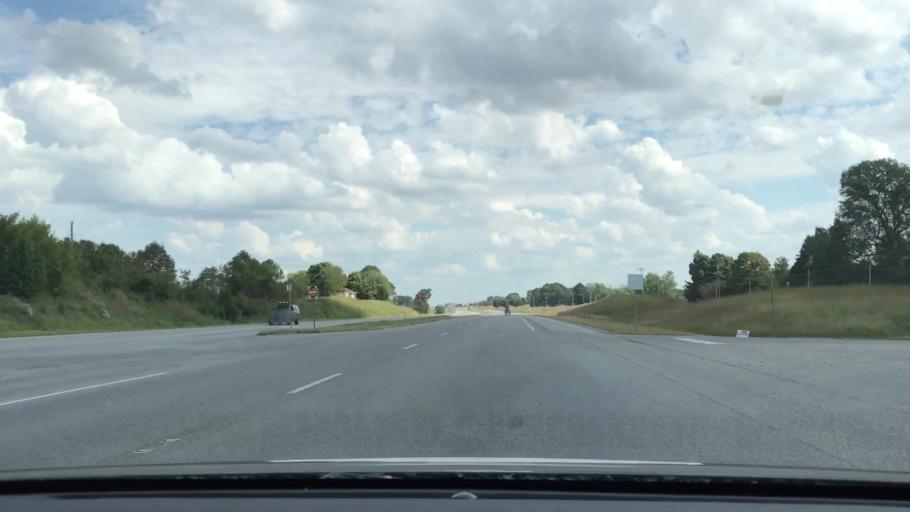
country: US
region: Kentucky
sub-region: Trigg County
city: Cadiz
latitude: 36.8699
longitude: -87.7698
